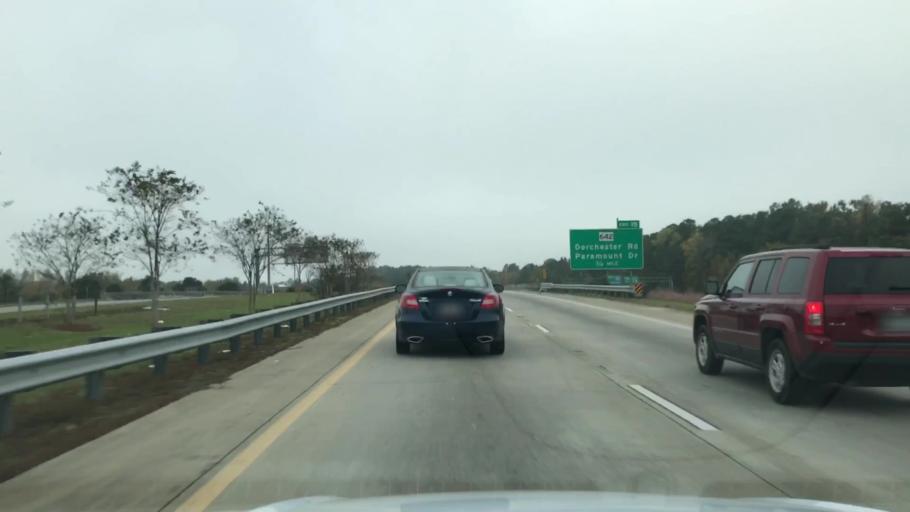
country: US
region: South Carolina
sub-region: Berkeley County
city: Hanahan
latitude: 32.8698
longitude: -80.0273
